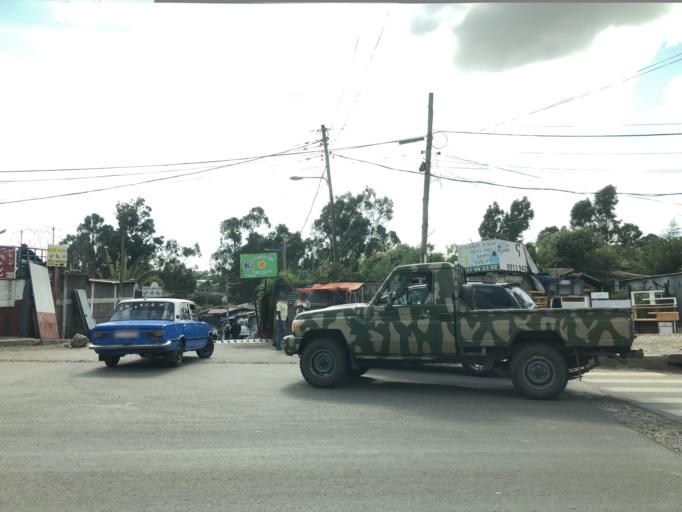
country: ET
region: Adis Abeba
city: Addis Ababa
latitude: 9.0228
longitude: 38.7810
